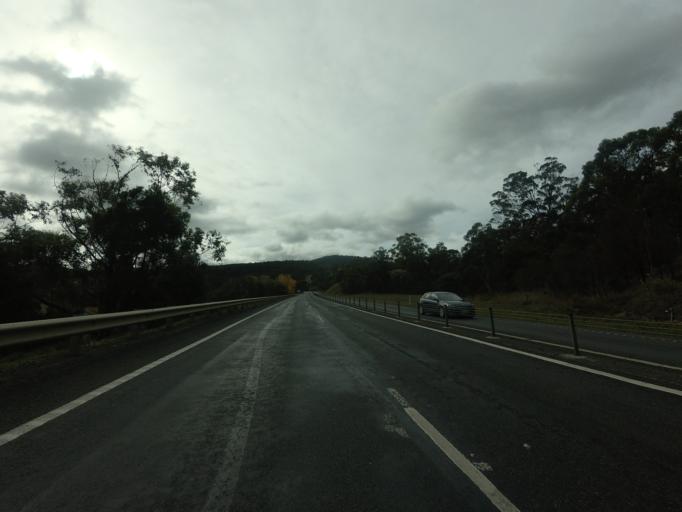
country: AU
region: Tasmania
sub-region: Brighton
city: Bridgewater
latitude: -42.5855
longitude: 147.2262
